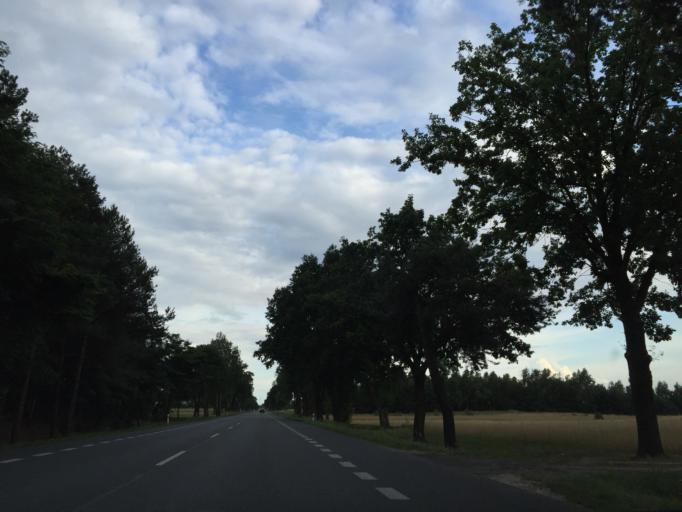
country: PL
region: Lublin Voivodeship
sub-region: Powiat lubartowski
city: Firlej
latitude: 51.5898
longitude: 22.4817
